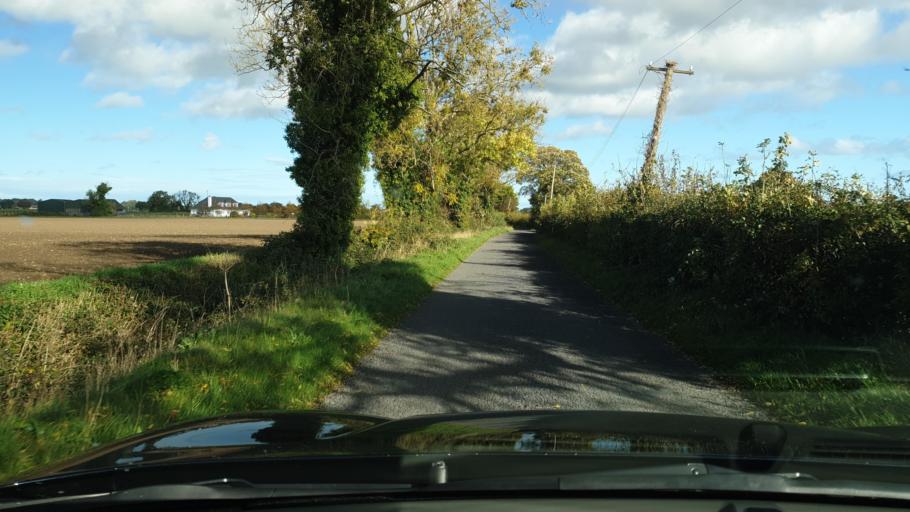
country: IE
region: Leinster
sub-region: Fingal County
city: Swords
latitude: 53.4938
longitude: -6.2514
